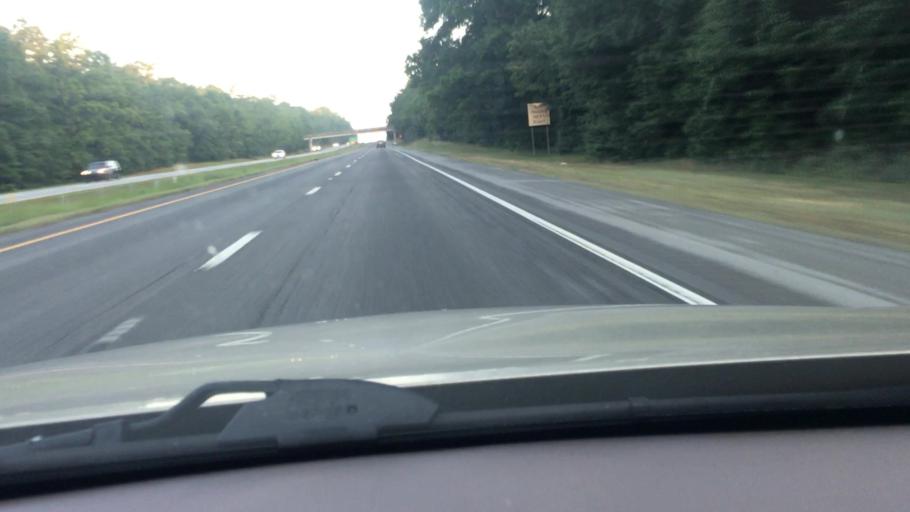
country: US
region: South Carolina
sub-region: Richland County
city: Lake Murray of Richland
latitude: 34.1585
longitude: -81.2696
